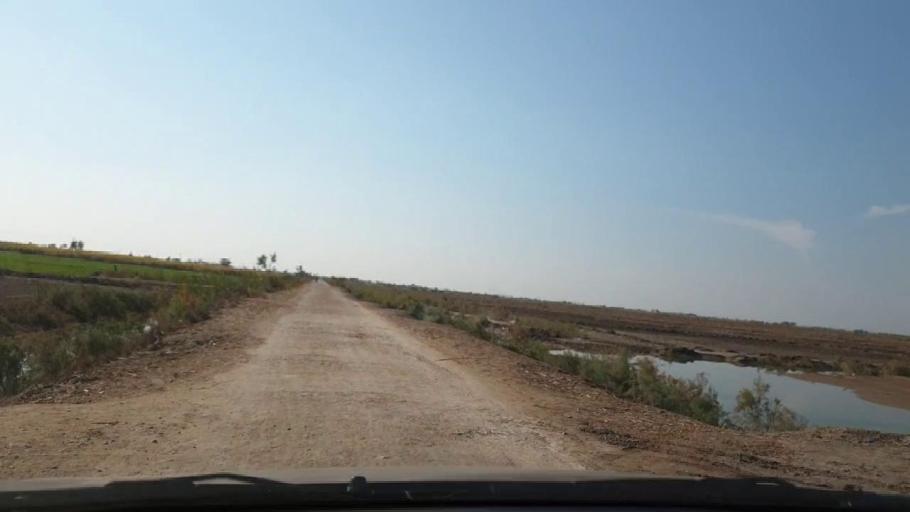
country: PK
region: Sindh
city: Khadro
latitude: 26.1563
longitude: 68.7948
